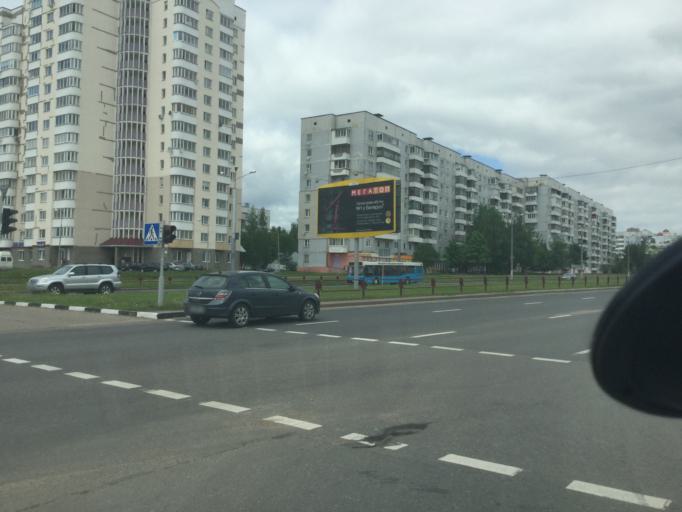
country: BY
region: Vitebsk
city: Vitebsk
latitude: 55.1620
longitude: 30.2220
